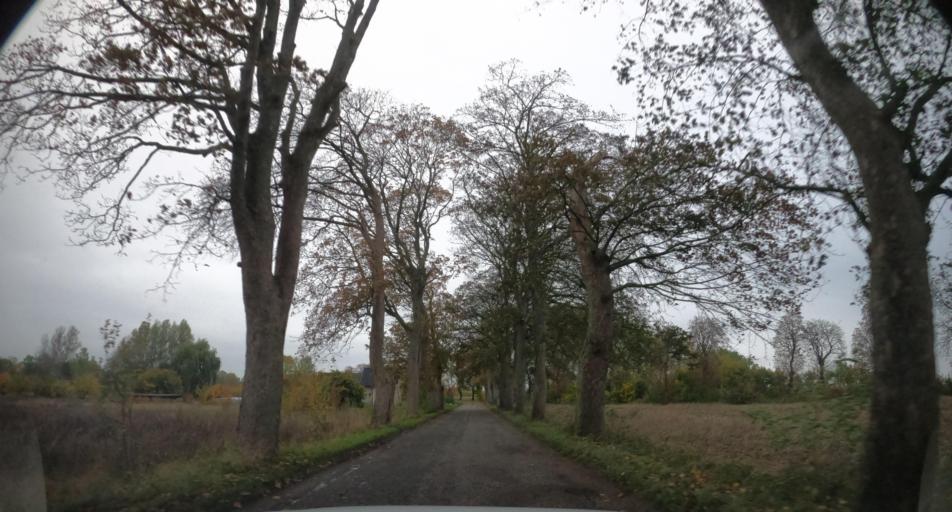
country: PL
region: West Pomeranian Voivodeship
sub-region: Powiat kamienski
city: Wolin
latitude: 53.9117
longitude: 14.6153
